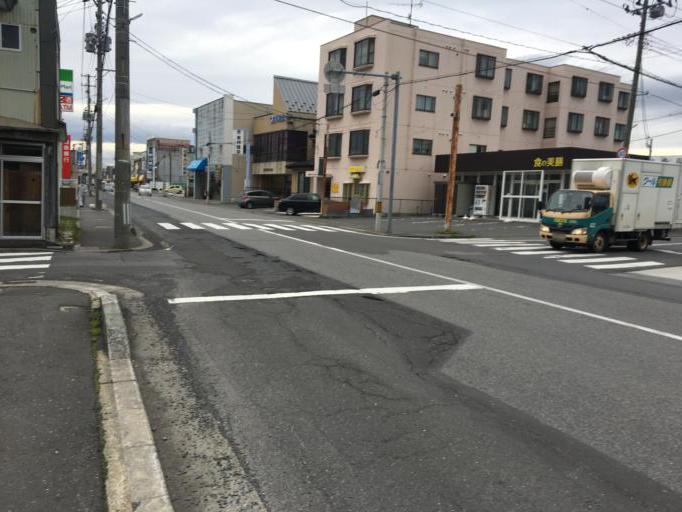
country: JP
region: Aomori
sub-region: Hachinohe Shi
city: Uchimaru
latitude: 40.5230
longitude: 141.5212
